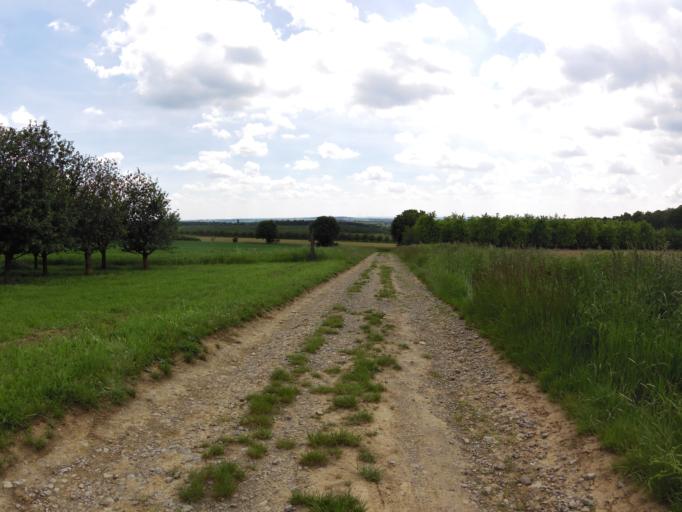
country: DE
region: Bavaria
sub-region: Regierungsbezirk Unterfranken
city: Sommerhausen
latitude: 49.7160
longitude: 10.0347
